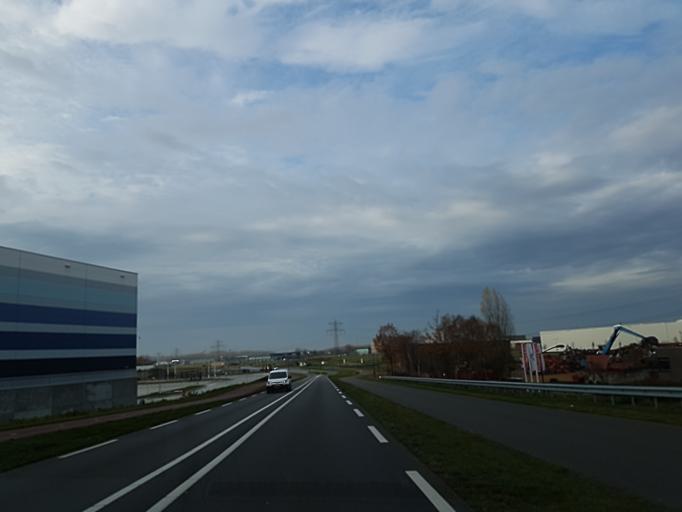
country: NL
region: North Brabant
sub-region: Roosendaal
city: Roosendaal
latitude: 51.5592
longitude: 4.4826
